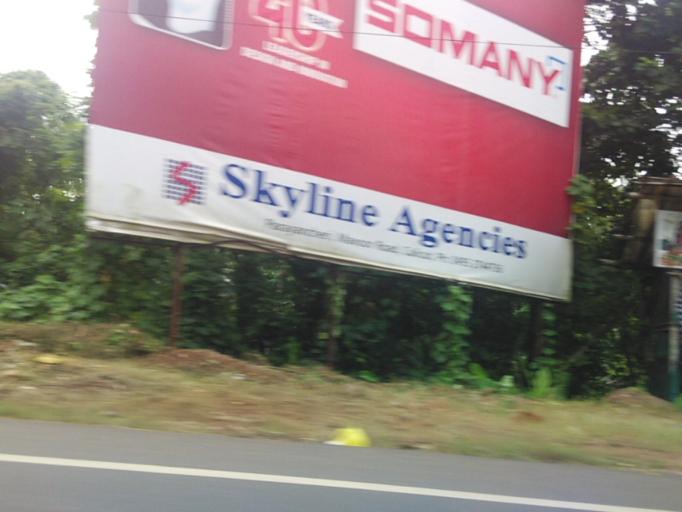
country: IN
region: Kerala
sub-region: Kozhikode
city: Kunnamangalam
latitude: 11.3000
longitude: 75.8557
